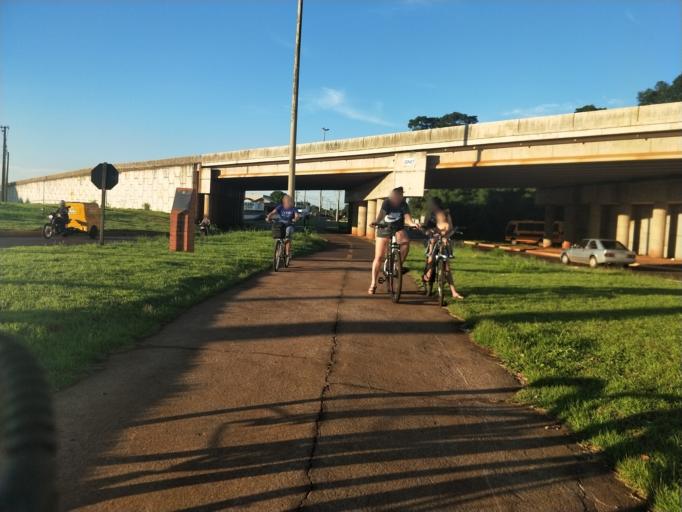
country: BR
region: Parana
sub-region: Marechal Candido Rondon
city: Marechal Candido Rondon
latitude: -24.5464
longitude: -54.0442
